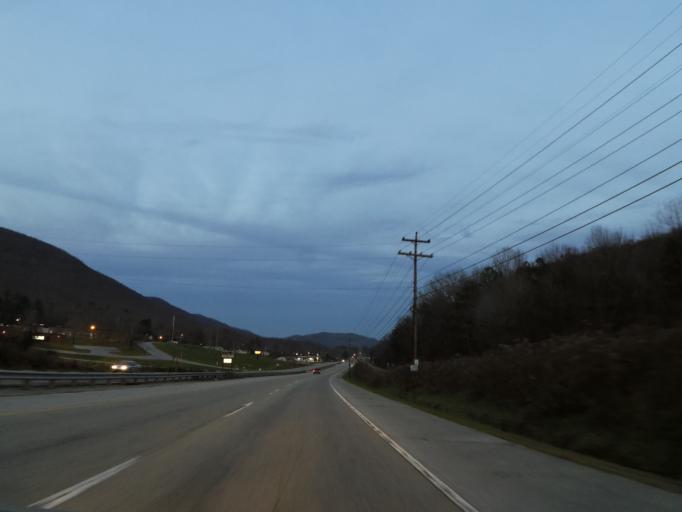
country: US
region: Tennessee
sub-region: Roane County
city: Harriman
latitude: 35.9634
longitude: -84.5204
